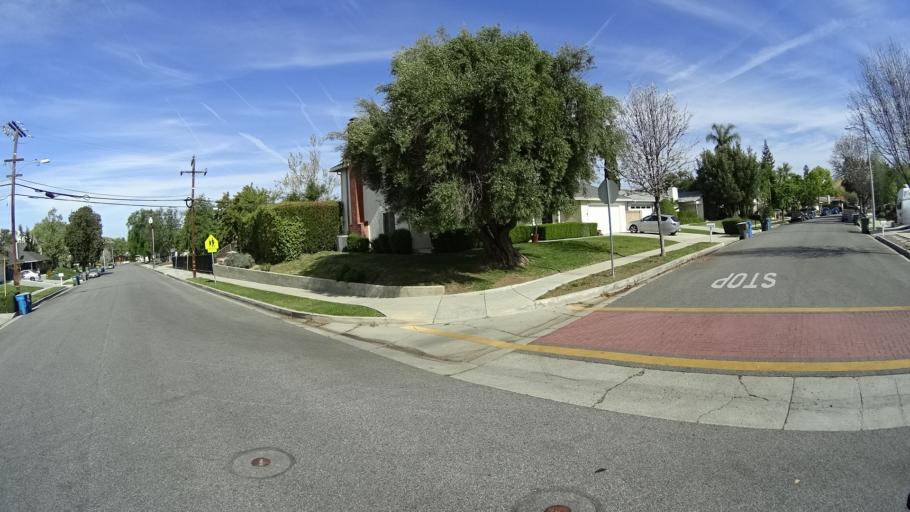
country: US
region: California
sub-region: Ventura County
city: Thousand Oaks
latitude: 34.1966
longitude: -118.8752
